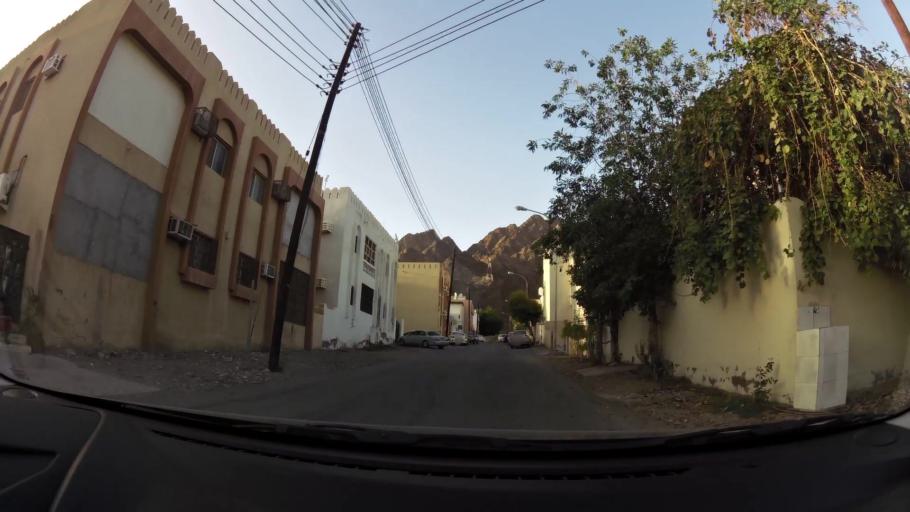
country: OM
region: Muhafazat Masqat
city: Muscat
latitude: 23.5754
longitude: 58.5751
